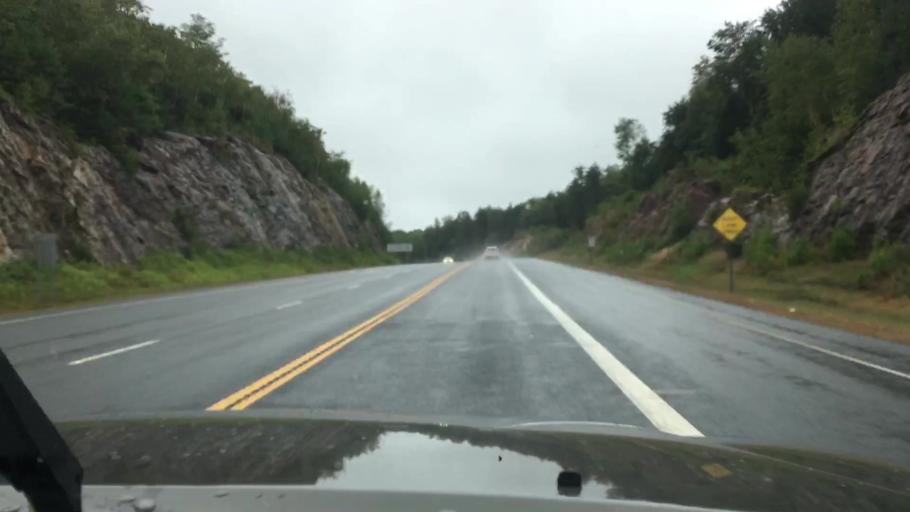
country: US
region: New Hampshire
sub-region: Cheshire County
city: Harrisville
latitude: 43.0067
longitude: -72.1620
